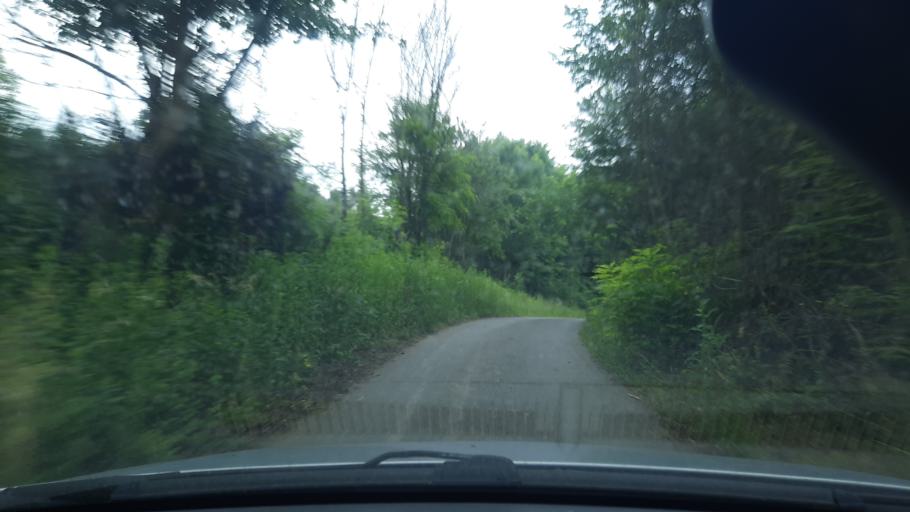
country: RS
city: Jarebice
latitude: 44.5145
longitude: 19.4782
